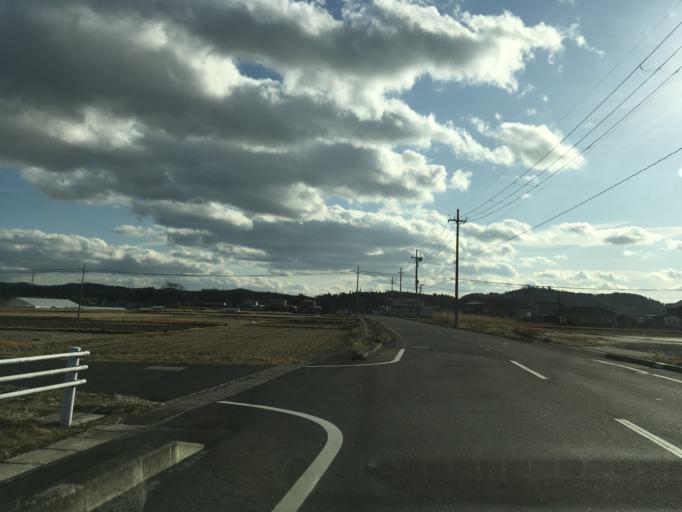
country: JP
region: Iwate
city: Ichinoseki
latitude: 38.8298
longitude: 140.9989
